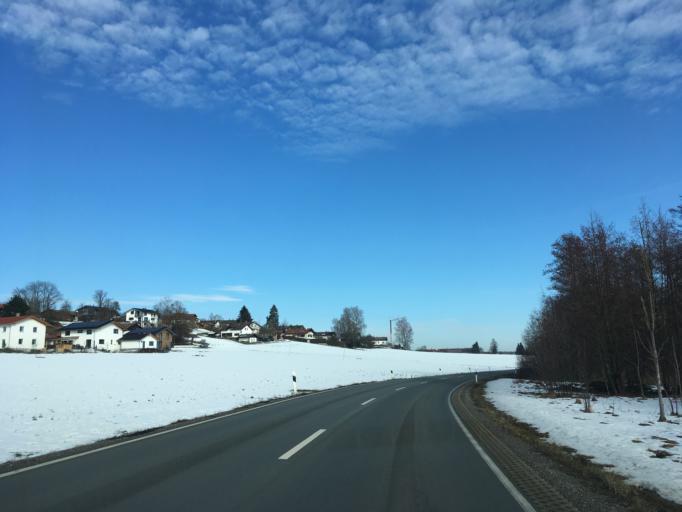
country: DE
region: Bavaria
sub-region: Upper Bavaria
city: Rosenheim
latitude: 47.8883
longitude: 12.1543
